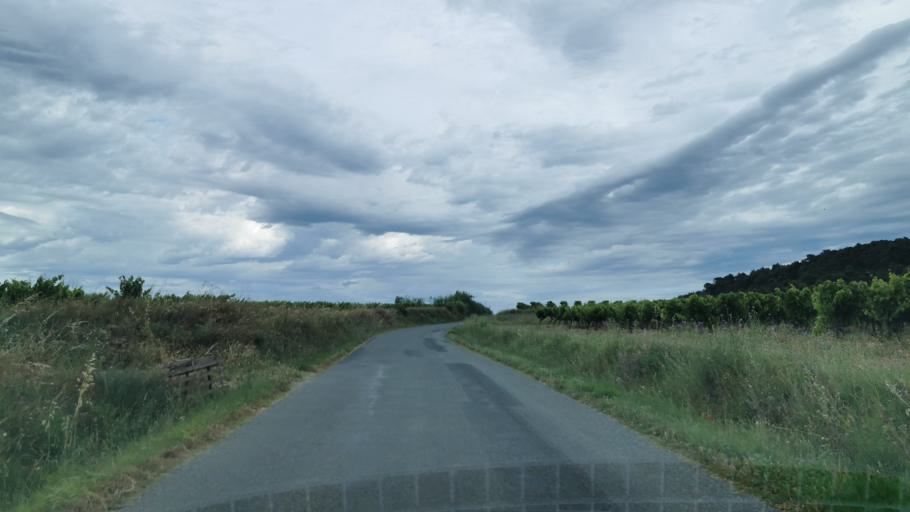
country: FR
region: Languedoc-Roussillon
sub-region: Departement de l'Aude
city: Moussan
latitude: 43.2234
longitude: 2.9384
